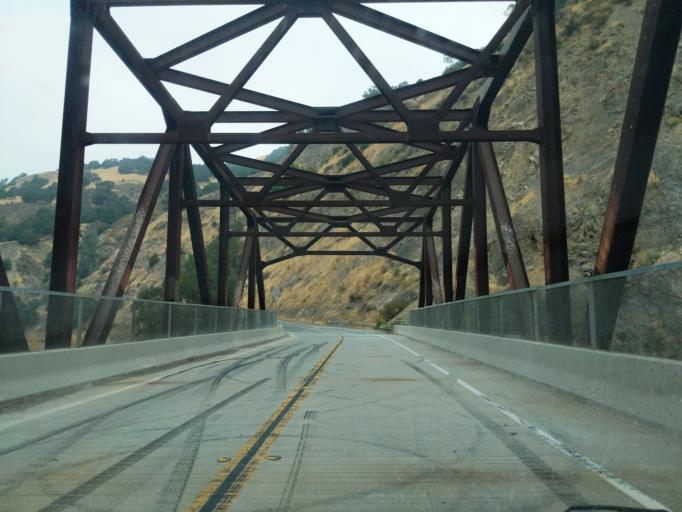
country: US
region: California
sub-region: Santa Clara County
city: San Martin
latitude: 37.1534
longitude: -121.5818
